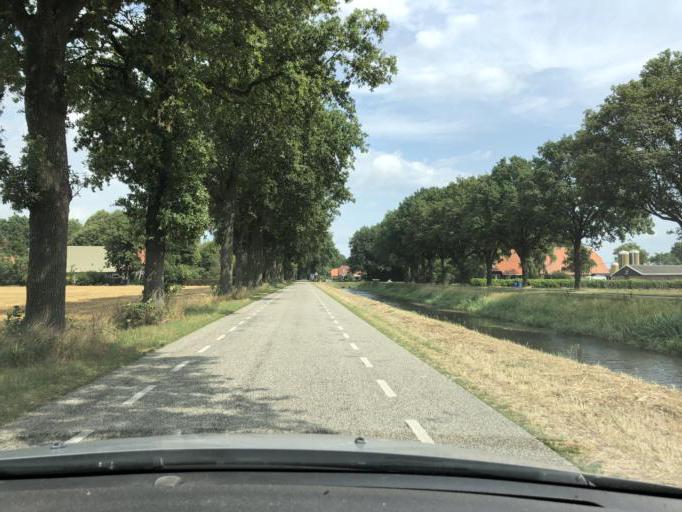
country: NL
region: Drenthe
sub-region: Gemeente Coevorden
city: Dalen
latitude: 52.8033
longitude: 6.6541
